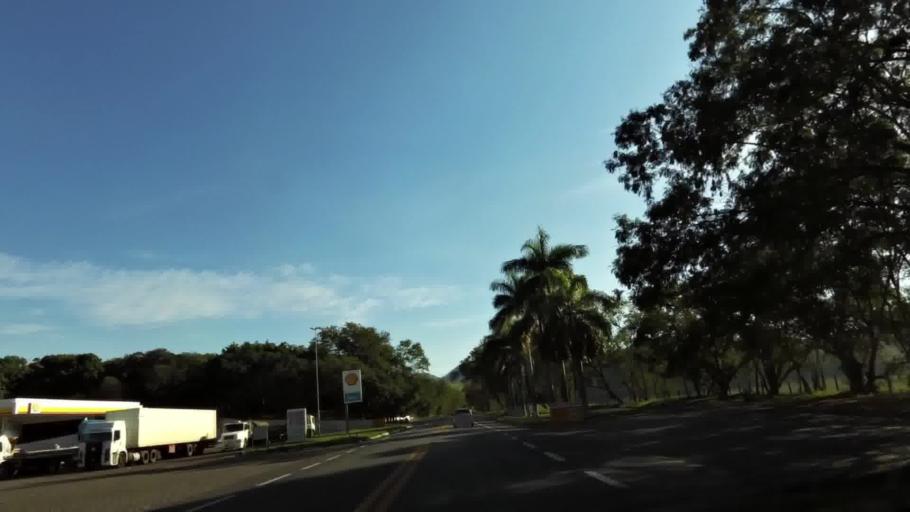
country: BR
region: Espirito Santo
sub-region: Viana
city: Viana
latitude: -20.4106
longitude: -40.4589
